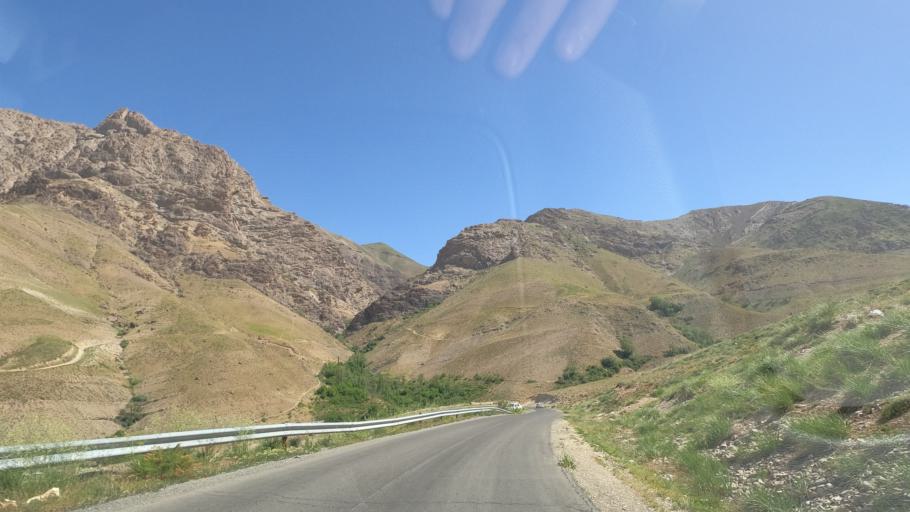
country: IR
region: Alborz
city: Karaj
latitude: 35.9232
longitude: 51.1570
